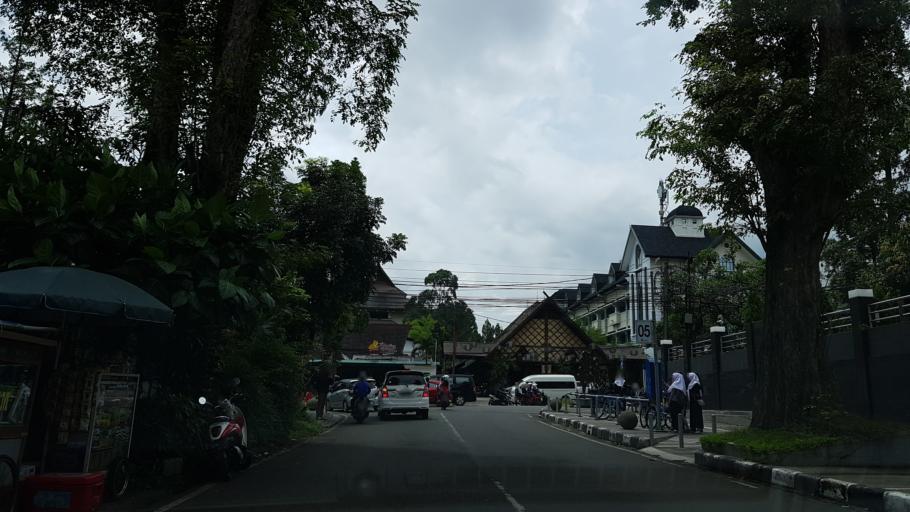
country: ID
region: West Java
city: Bandung
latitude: -6.8916
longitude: 107.6137
